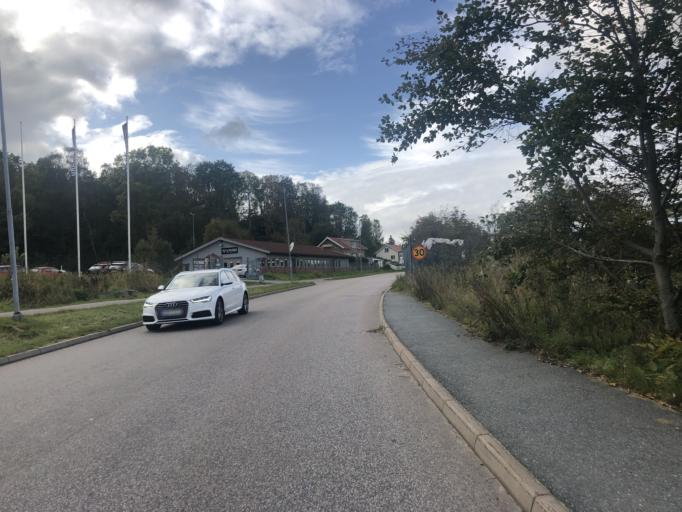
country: SE
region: Vaestra Goetaland
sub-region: Molndal
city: Moelndal
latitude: 57.6415
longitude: 11.9830
